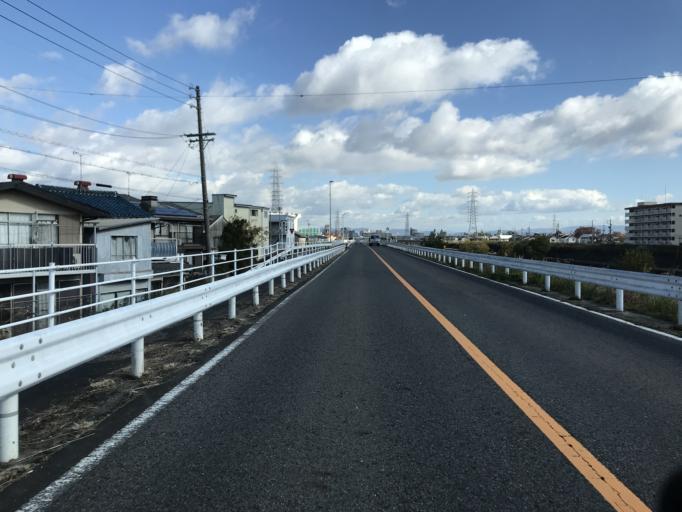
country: JP
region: Aichi
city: Nagoya-shi
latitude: 35.2320
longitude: 136.8918
